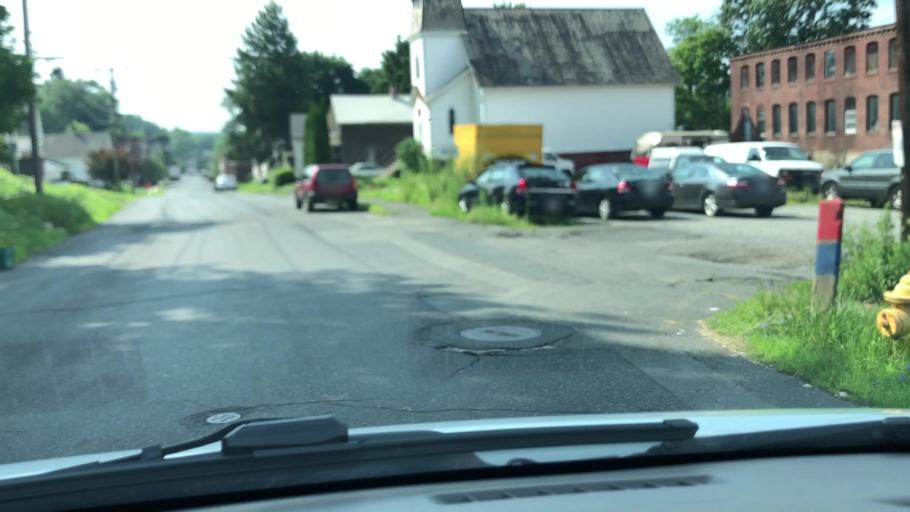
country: US
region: Massachusetts
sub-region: Franklin County
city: Greenfield
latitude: 42.5847
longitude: -72.5992
